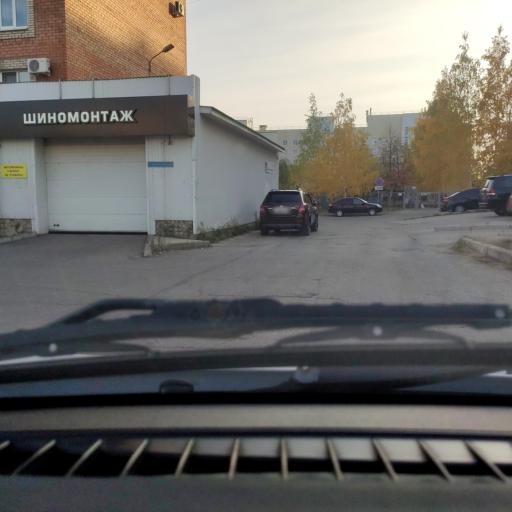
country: RU
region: Samara
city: Zhigulevsk
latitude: 53.4744
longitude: 49.4704
